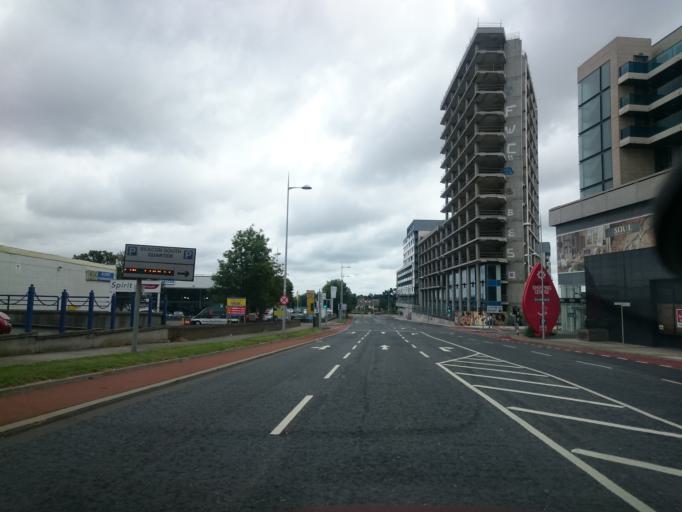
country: IE
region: Leinster
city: Sandyford
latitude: 53.2785
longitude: -6.2170
